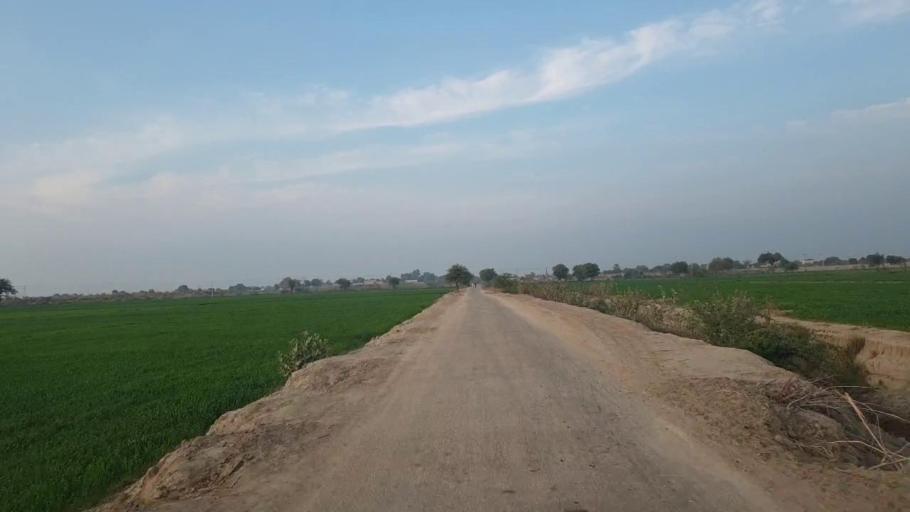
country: PK
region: Sindh
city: Shahpur Chakar
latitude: 26.1153
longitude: 68.5465
